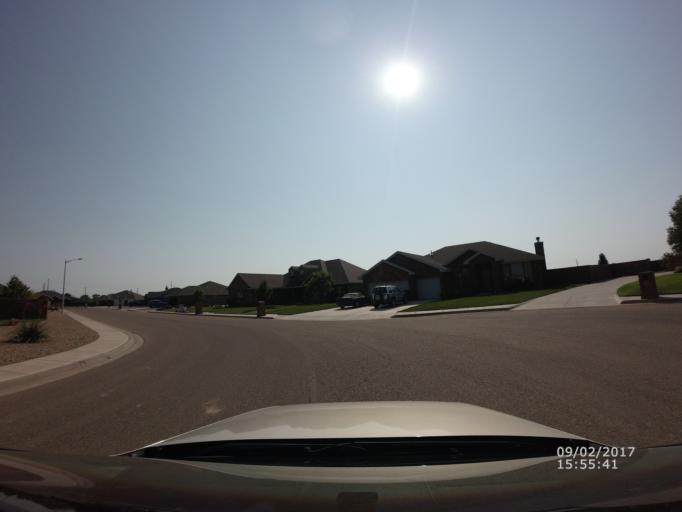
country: US
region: New Mexico
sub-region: Curry County
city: Clovis
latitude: 34.4500
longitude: -103.1899
